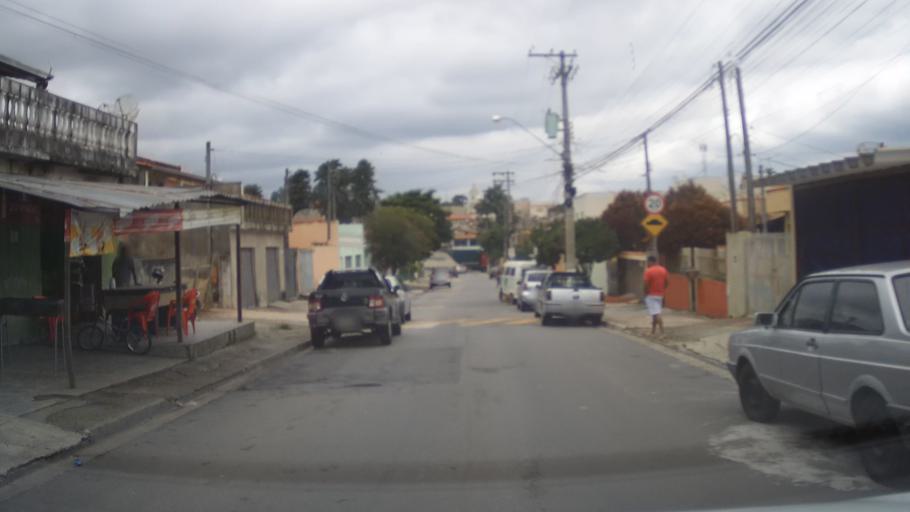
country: BR
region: Sao Paulo
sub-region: Louveira
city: Louveira
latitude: -23.0825
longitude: -46.9798
